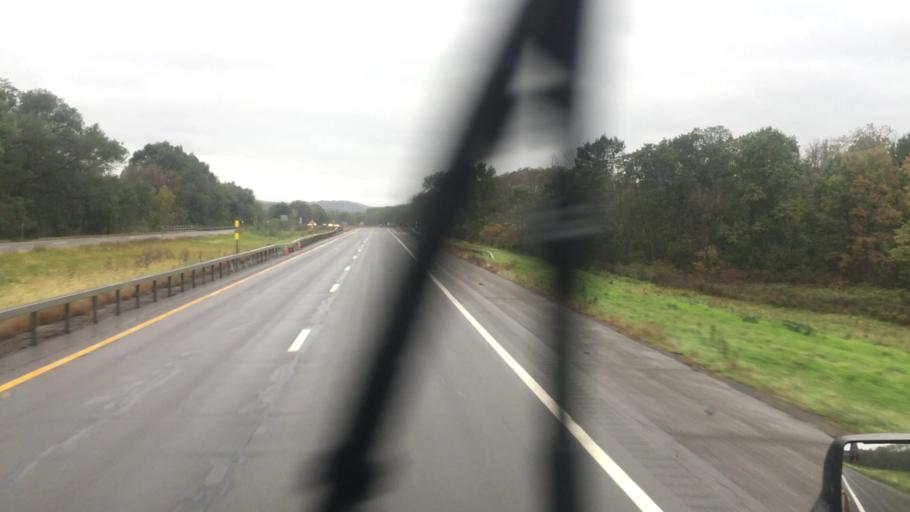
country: US
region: New York
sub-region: Tioga County
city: Apalachin
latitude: 42.0695
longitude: -76.1013
